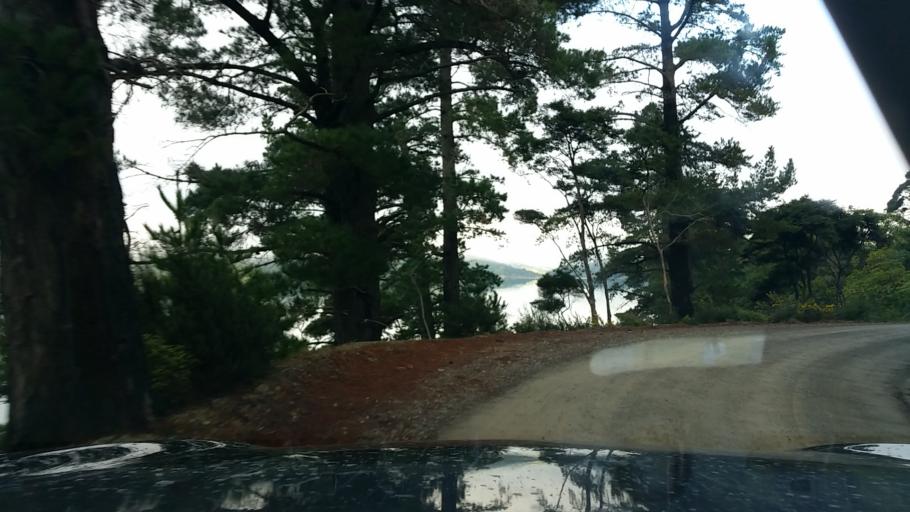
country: NZ
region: Marlborough
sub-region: Marlborough District
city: Picton
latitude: -41.1783
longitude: 174.0650
